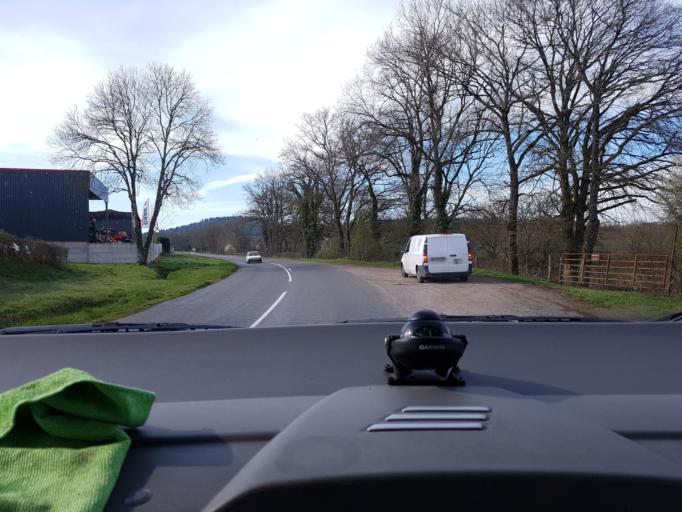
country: FR
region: Bourgogne
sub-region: Departement de Saone-et-Loire
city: Toulon-sur-Arroux
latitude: 46.7304
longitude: 4.1300
